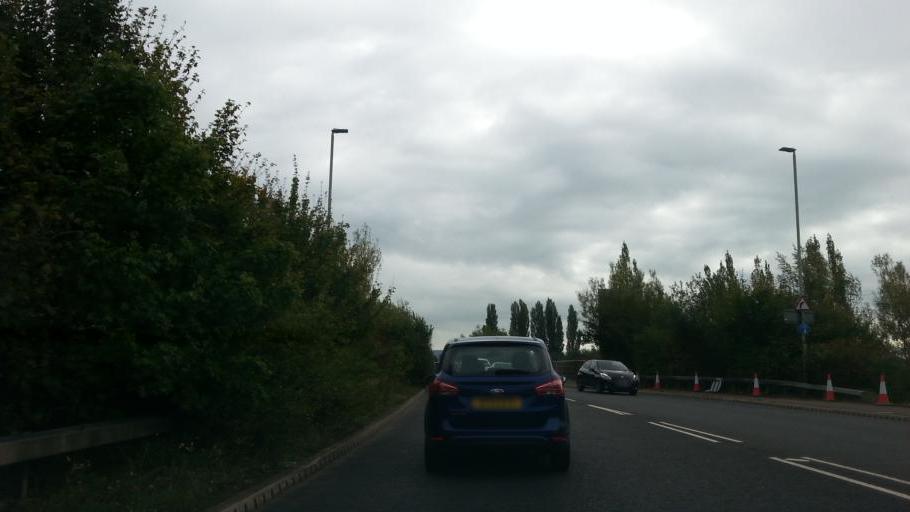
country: GB
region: England
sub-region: Gloucestershire
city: Gloucester
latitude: 51.8693
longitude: -2.2593
